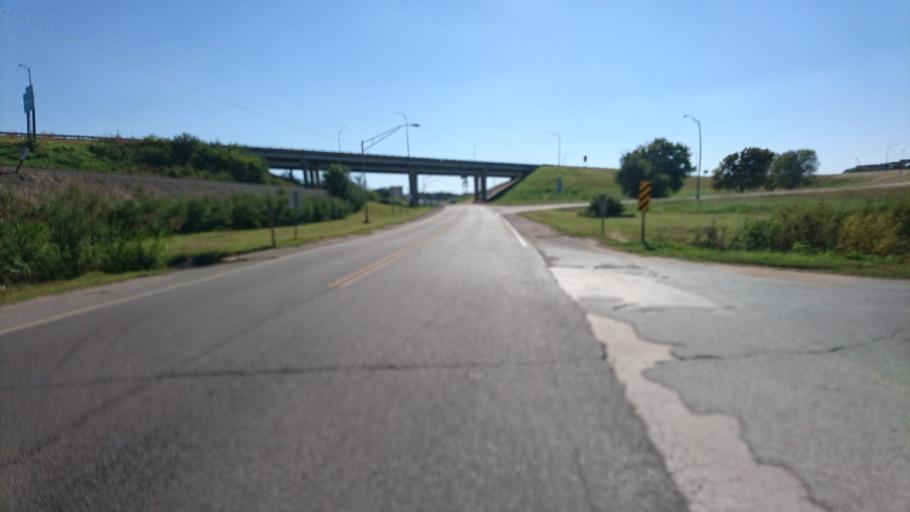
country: US
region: Oklahoma
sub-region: Custer County
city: Clinton
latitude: 35.5004
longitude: -98.9756
